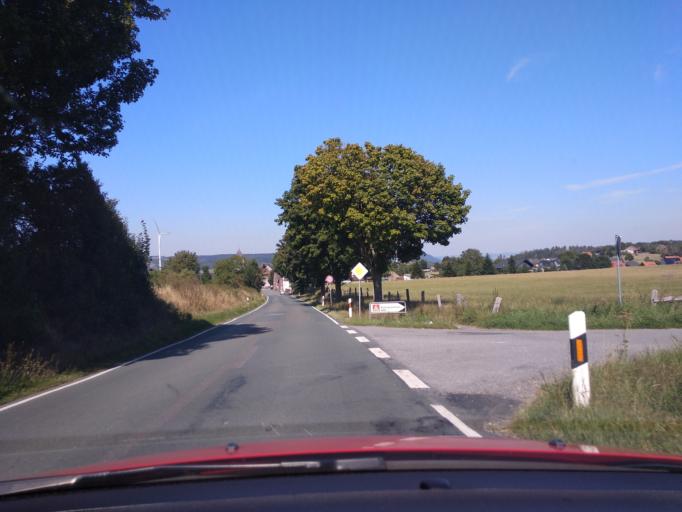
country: DE
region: North Rhine-Westphalia
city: Beverungen
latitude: 51.6790
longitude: 9.3104
